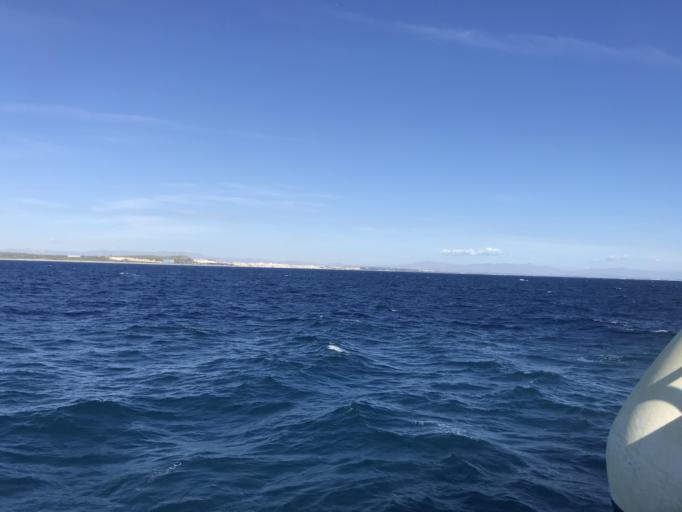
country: ES
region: Valencia
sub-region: Provincia de Alicante
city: Guardamar del Segura
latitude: 38.0286
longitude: -0.6162
